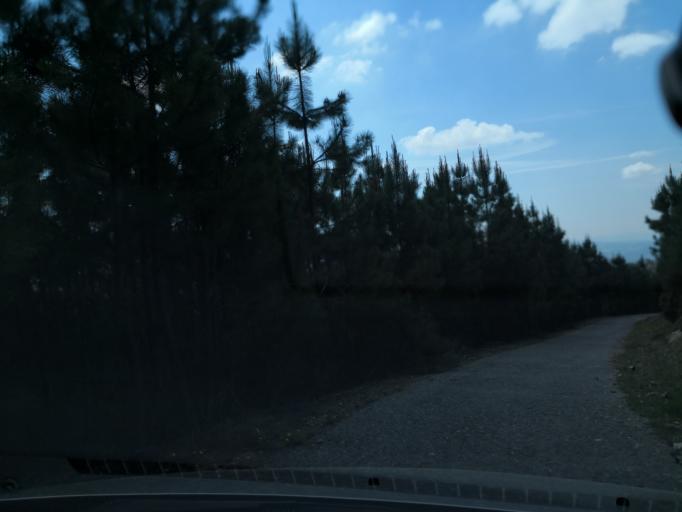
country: PT
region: Vila Real
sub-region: Vila Real
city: Vila Real
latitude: 41.3625
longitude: -7.7372
